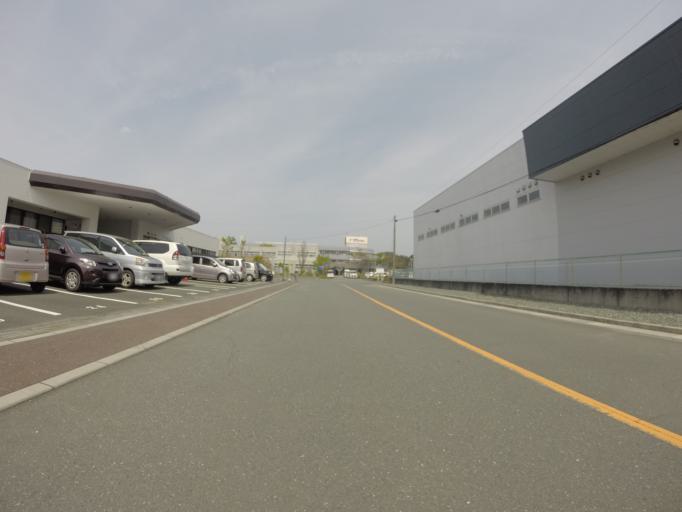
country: JP
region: Shizuoka
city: Kakegawa
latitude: 34.7749
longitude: 137.9887
